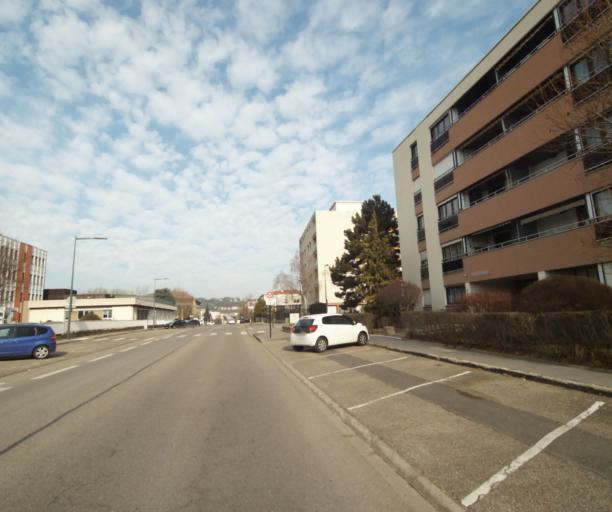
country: FR
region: Lorraine
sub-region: Departement de Meurthe-et-Moselle
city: Villers-les-Nancy
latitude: 48.6738
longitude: 6.1596
